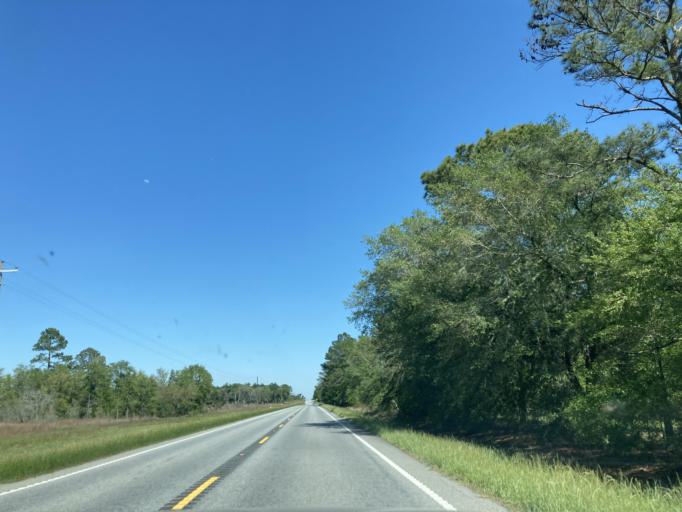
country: US
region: Georgia
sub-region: Miller County
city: Colquitt
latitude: 31.1861
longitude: -84.6236
